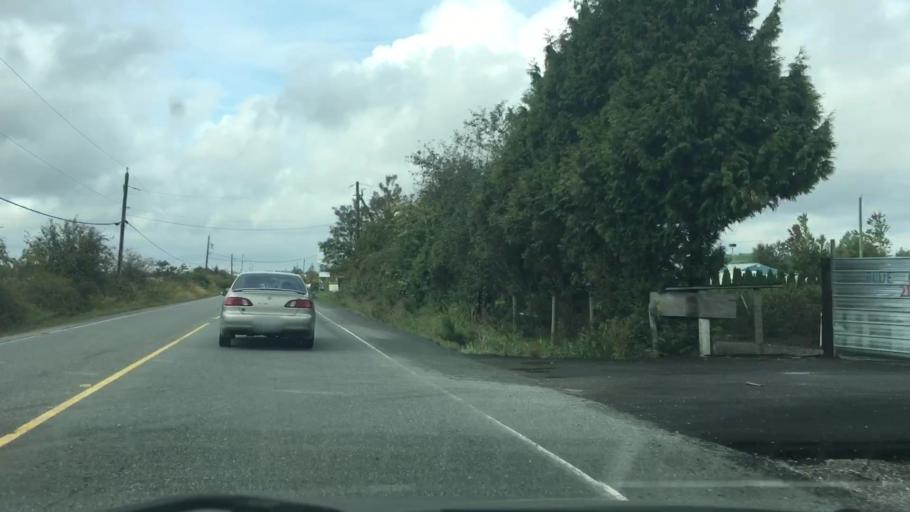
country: CA
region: British Columbia
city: Langley
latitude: 49.1041
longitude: -122.6154
